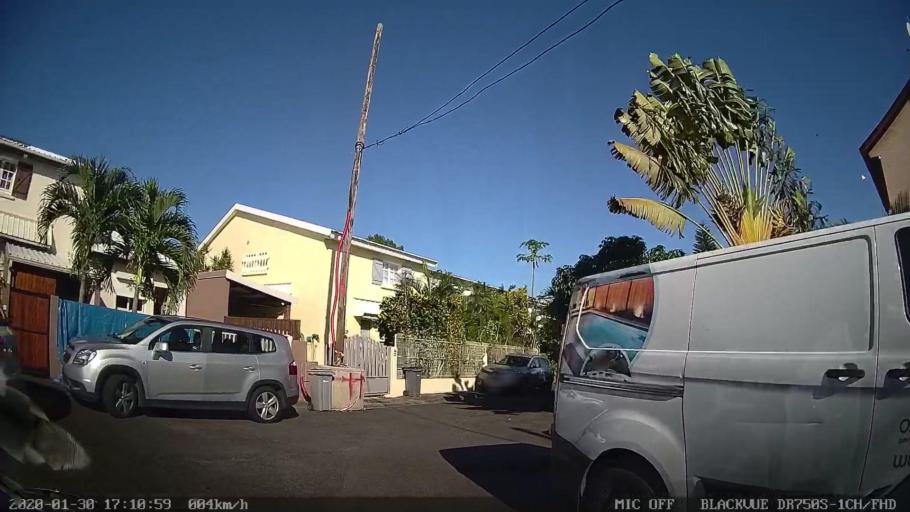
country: RE
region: Reunion
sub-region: Reunion
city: Sainte-Marie
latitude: -20.9143
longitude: 55.5129
